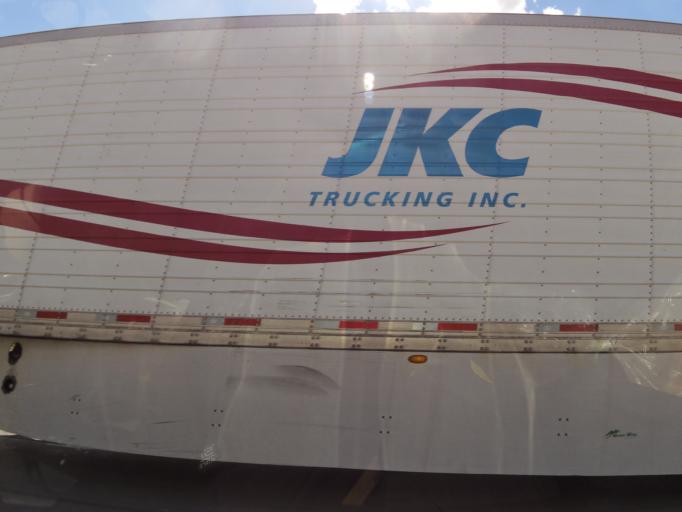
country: US
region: Iowa
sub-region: Johnson County
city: Tiffin
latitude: 41.6951
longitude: -91.6388
